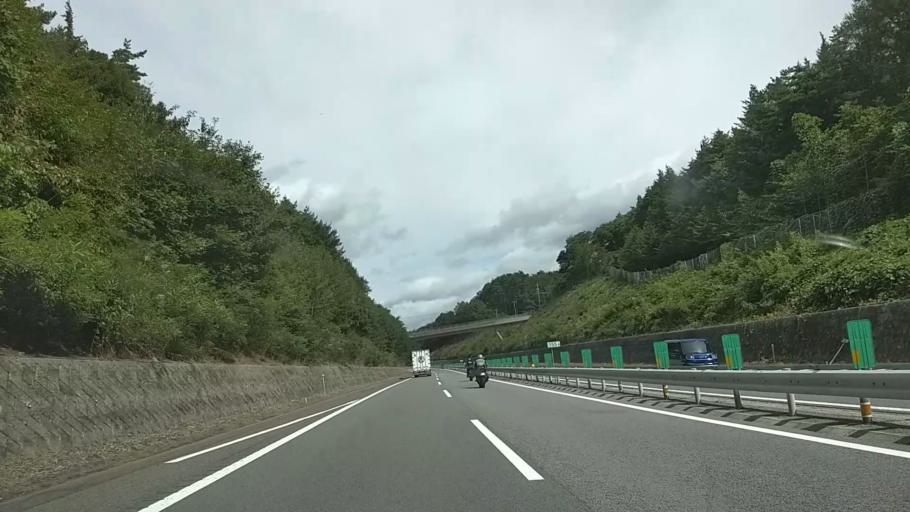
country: JP
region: Nagano
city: Chino
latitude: 35.9109
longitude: 138.2557
